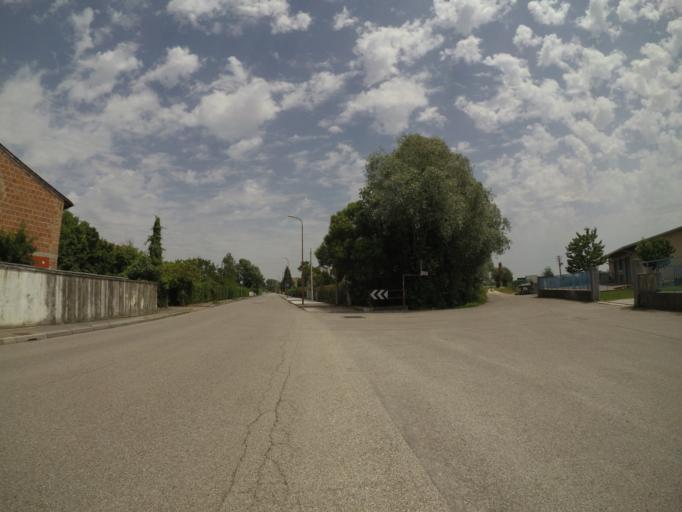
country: IT
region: Friuli Venezia Giulia
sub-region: Provincia di Udine
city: Camino al Tagliamento
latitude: 45.9268
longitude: 12.9495
